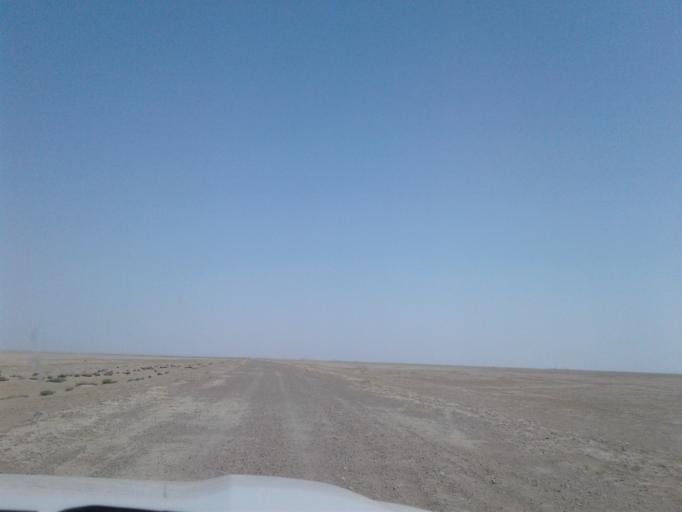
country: TM
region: Balkan
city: Gumdag
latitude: 38.3316
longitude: 54.5726
